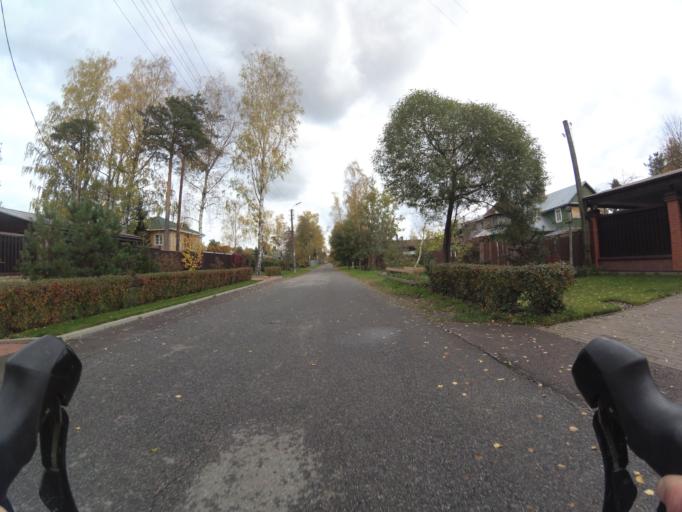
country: RU
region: St.-Petersburg
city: Lakhtinskiy
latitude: 59.9994
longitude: 30.1396
